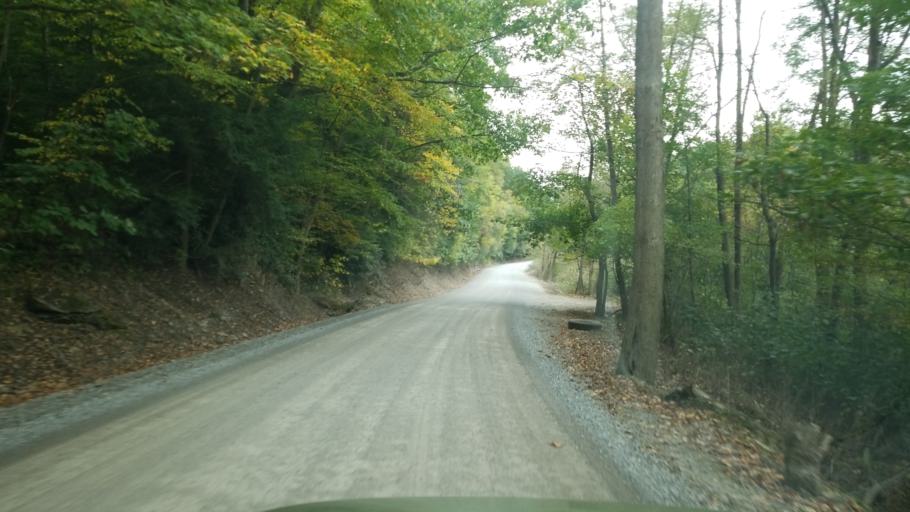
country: US
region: Pennsylvania
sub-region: Clearfield County
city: Curwensville
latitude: 40.9681
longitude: -78.4884
